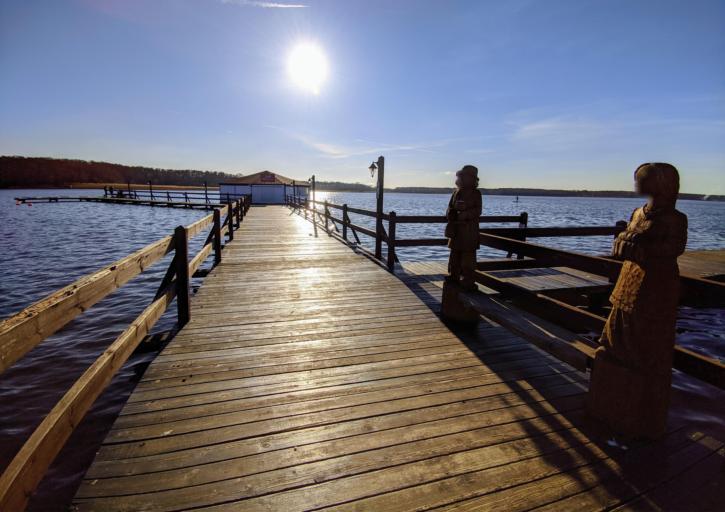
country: PL
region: Lubusz
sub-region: Powiat wschowski
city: Slawa
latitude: 51.8799
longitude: 16.0565
